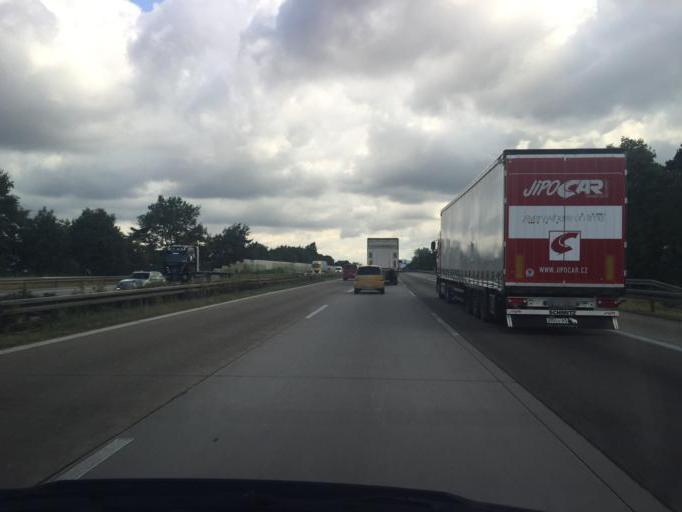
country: DE
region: Baden-Wuerttemberg
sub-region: Karlsruhe Region
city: Sankt Leon-Rot
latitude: 49.2582
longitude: 8.6033
